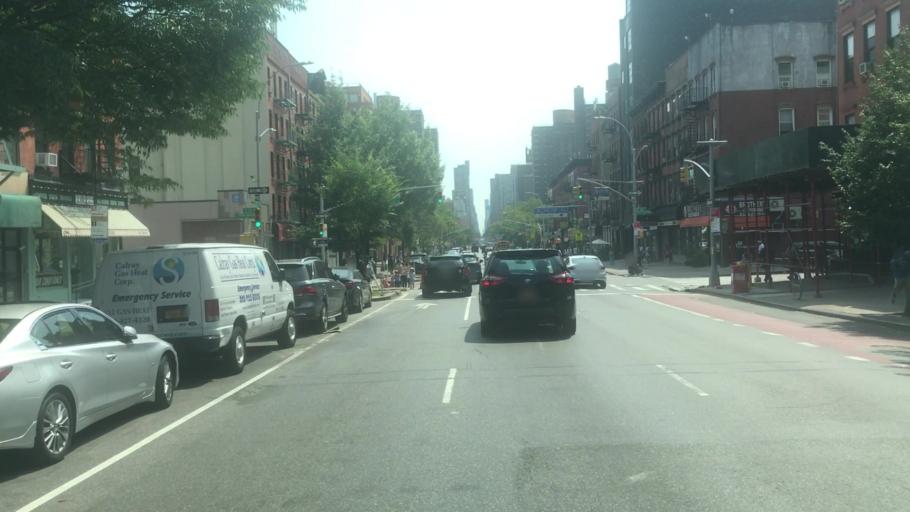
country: US
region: New York
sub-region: New York County
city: Manhattan
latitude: 40.7944
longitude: -73.9398
